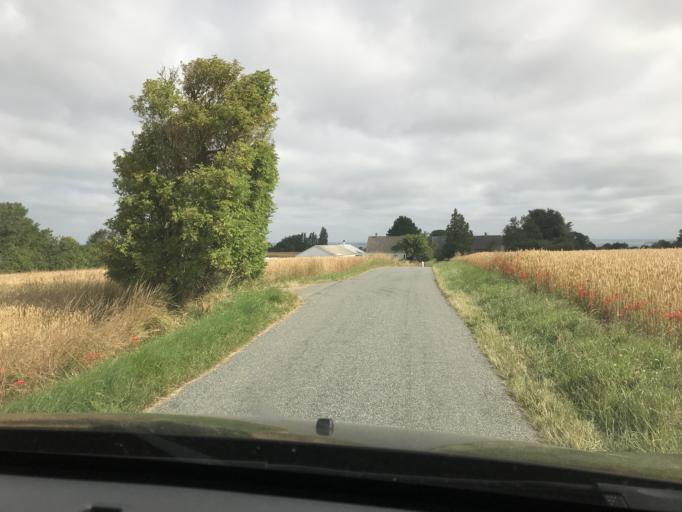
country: DK
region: South Denmark
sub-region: AEro Kommune
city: AEroskobing
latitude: 54.9278
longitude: 10.2798
